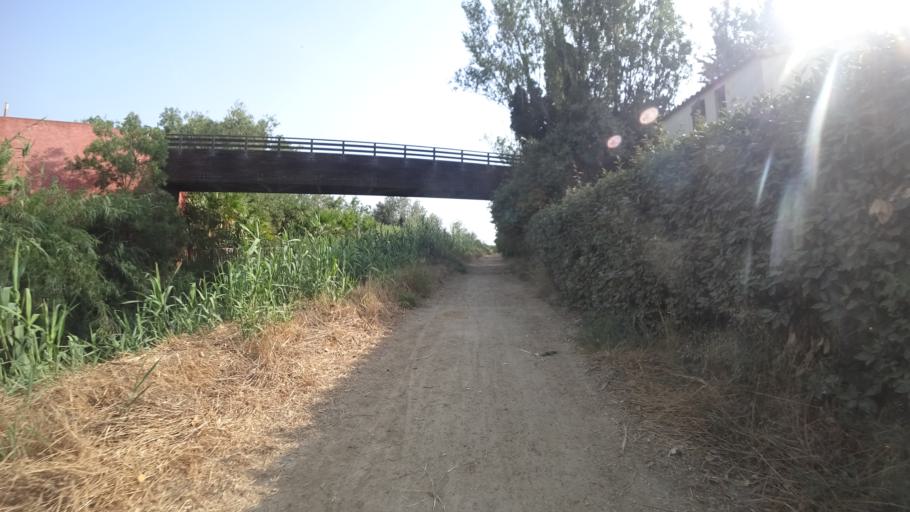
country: FR
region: Languedoc-Roussillon
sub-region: Departement des Pyrenees-Orientales
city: Sainte-Marie-Plage
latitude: 42.7402
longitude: 3.0315
